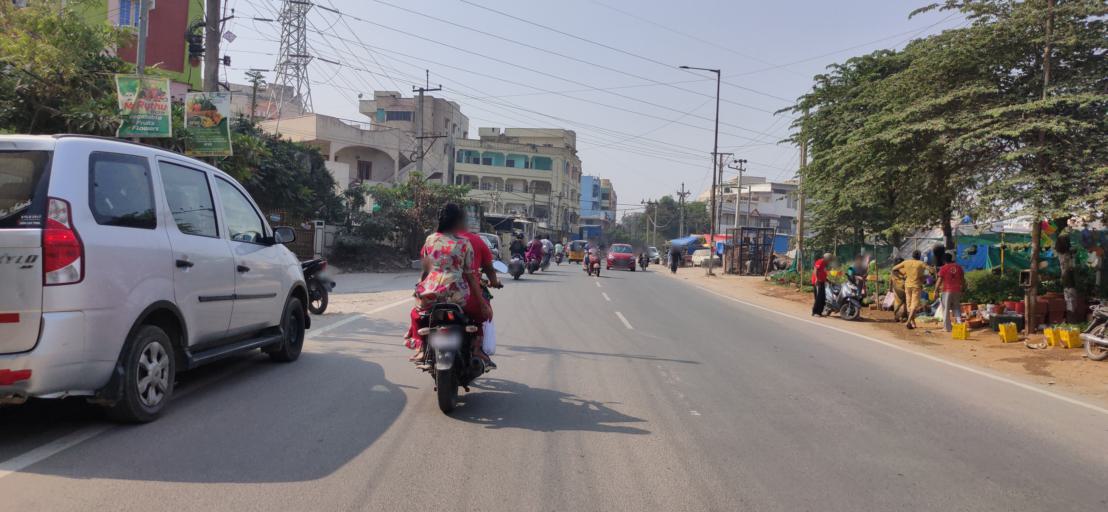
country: IN
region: Telangana
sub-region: Rangareddi
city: Kukatpalli
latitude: 17.5002
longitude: 78.4089
